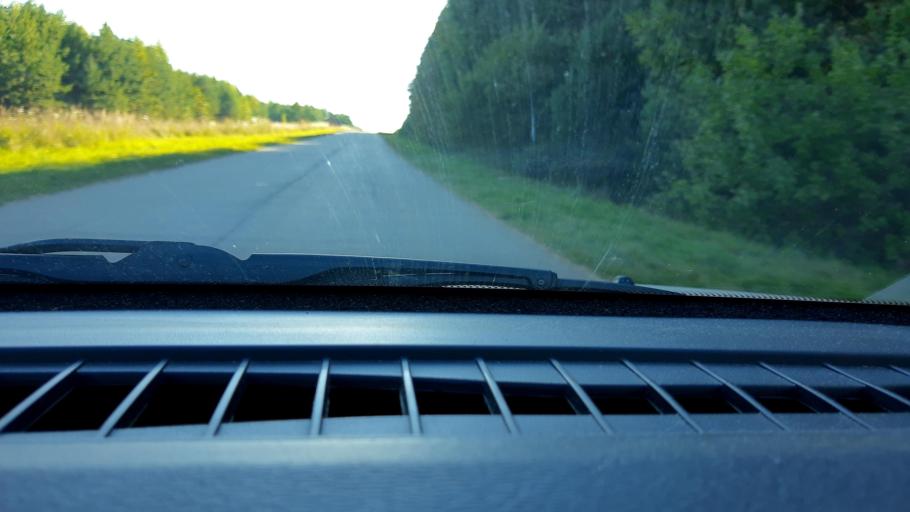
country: RU
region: Nizjnij Novgorod
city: Surovatikha
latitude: 55.9411
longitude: 43.9033
